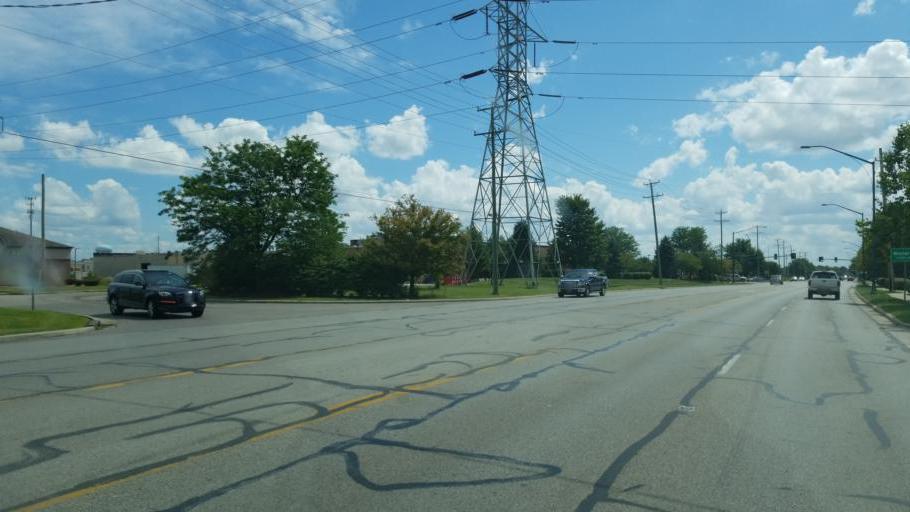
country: US
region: Ohio
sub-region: Franklin County
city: Westerville
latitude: 40.1514
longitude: -82.9211
